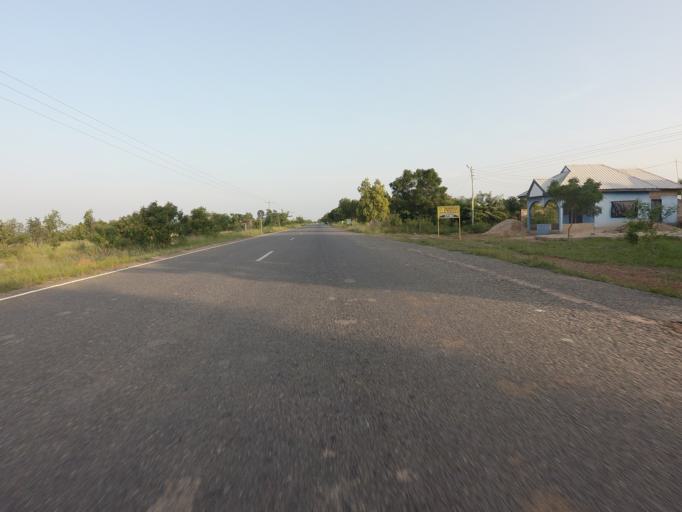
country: GH
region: Volta
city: Anloga
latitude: 5.9064
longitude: 0.7109
